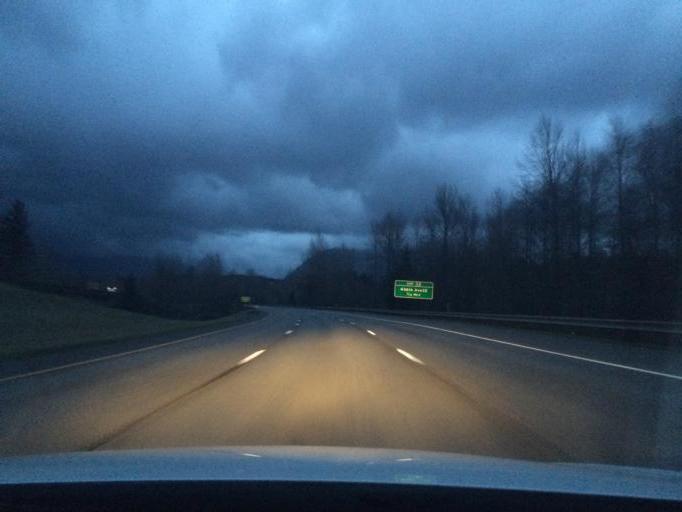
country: US
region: Washington
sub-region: King County
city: North Bend
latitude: 47.4742
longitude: -121.7816
